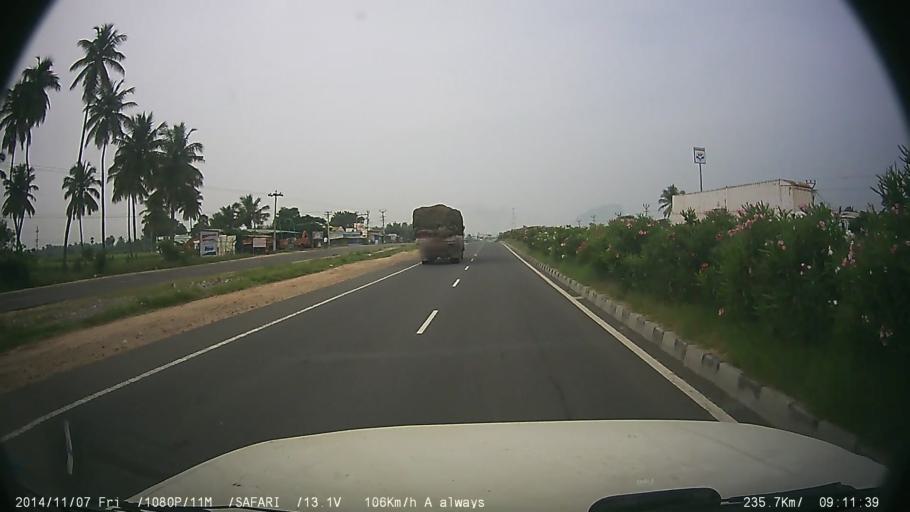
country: IN
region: Tamil Nadu
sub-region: Salem
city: Konganapuram
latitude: 11.4972
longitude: 77.9067
